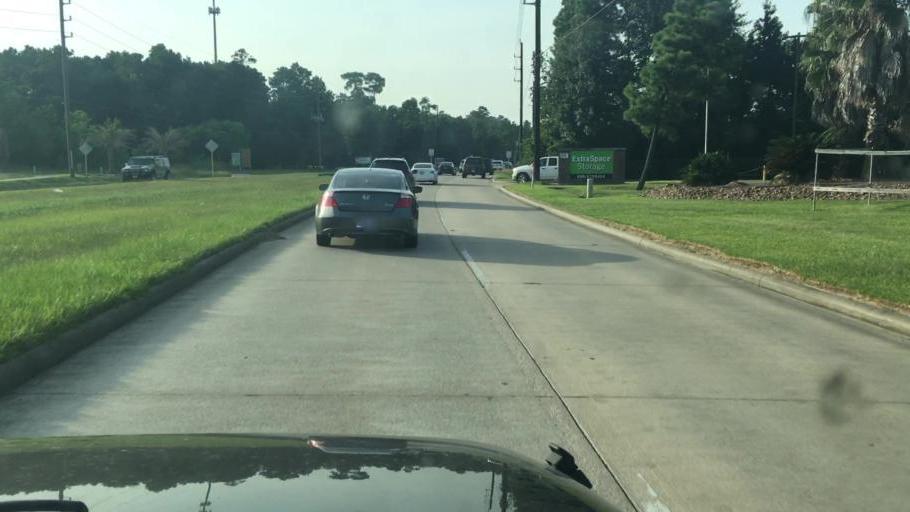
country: US
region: Texas
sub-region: Harris County
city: Atascocita
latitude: 29.9714
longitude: -95.1713
